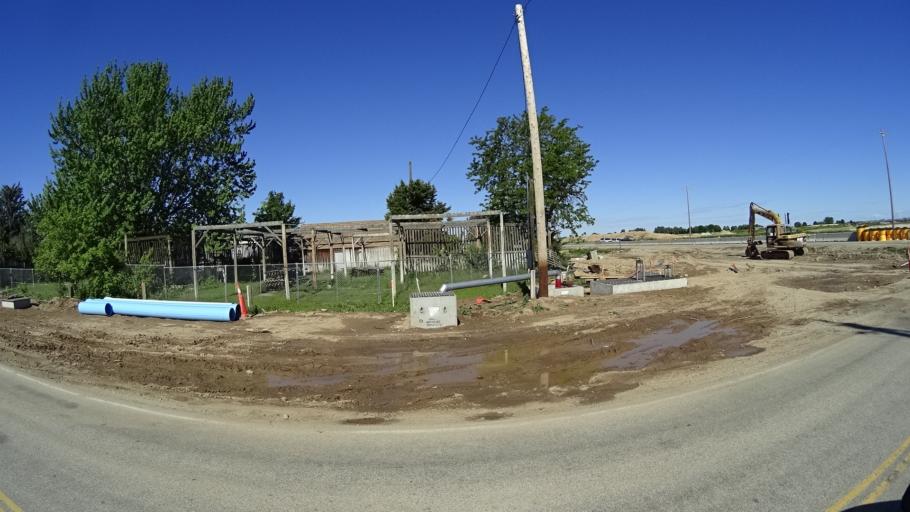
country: US
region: Idaho
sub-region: Ada County
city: Star
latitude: 43.6626
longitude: -116.4536
